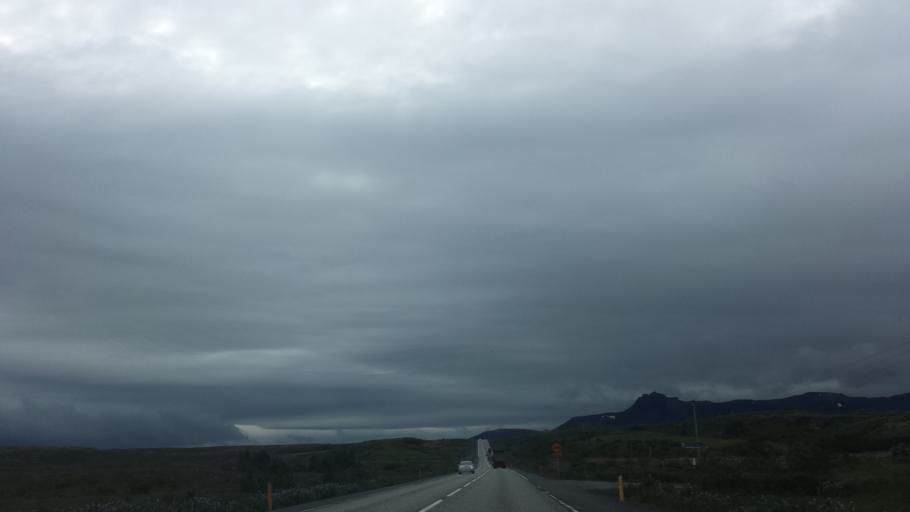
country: IS
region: Capital Region
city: Mosfellsbaer
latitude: 64.0808
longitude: -21.6683
